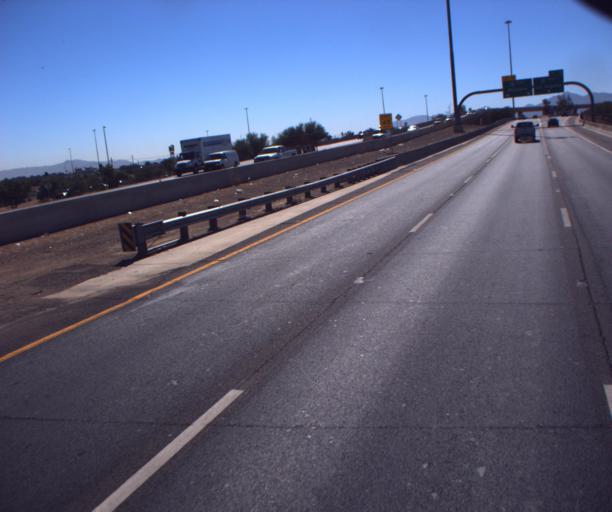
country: US
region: Arizona
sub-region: Maricopa County
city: Tolleson
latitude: 33.4665
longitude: -112.2688
